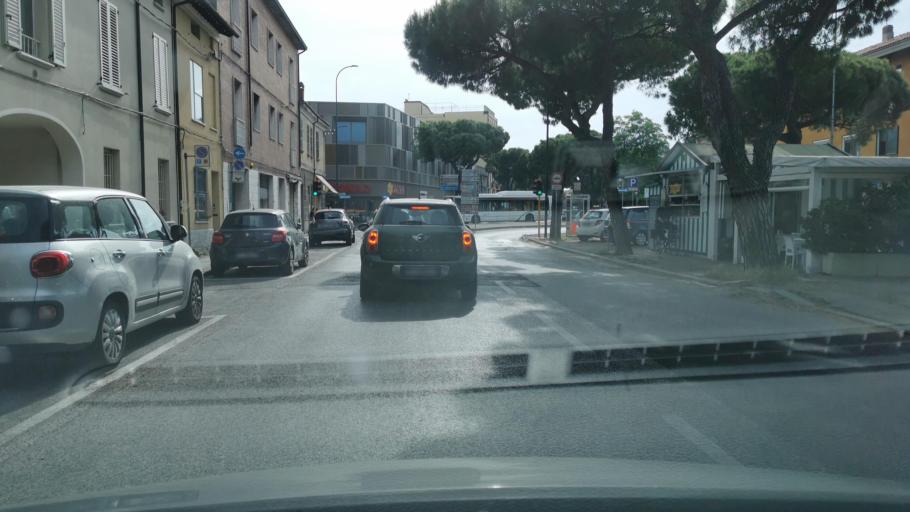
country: IT
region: Emilia-Romagna
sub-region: Provincia di Ravenna
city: Ravenna
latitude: 44.4117
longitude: 12.2075
